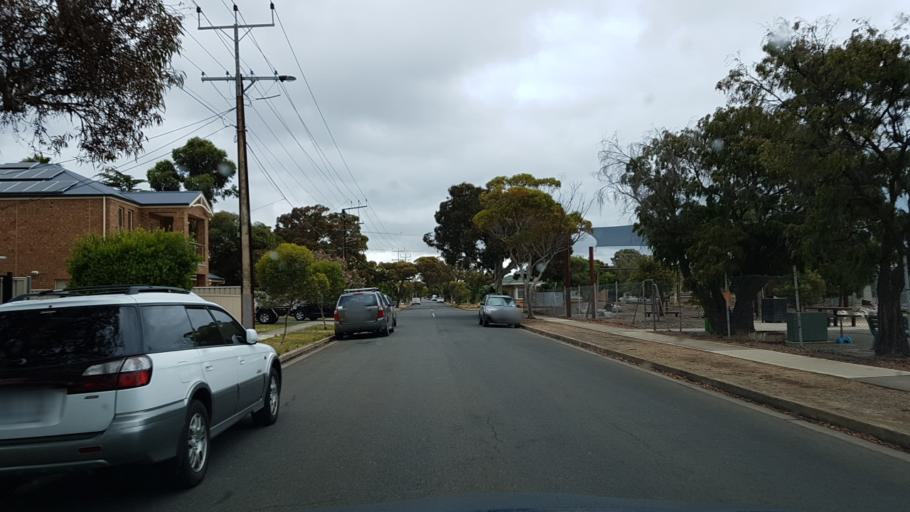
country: AU
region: South Australia
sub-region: Marion
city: South Plympton
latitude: -34.9726
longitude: 138.5489
